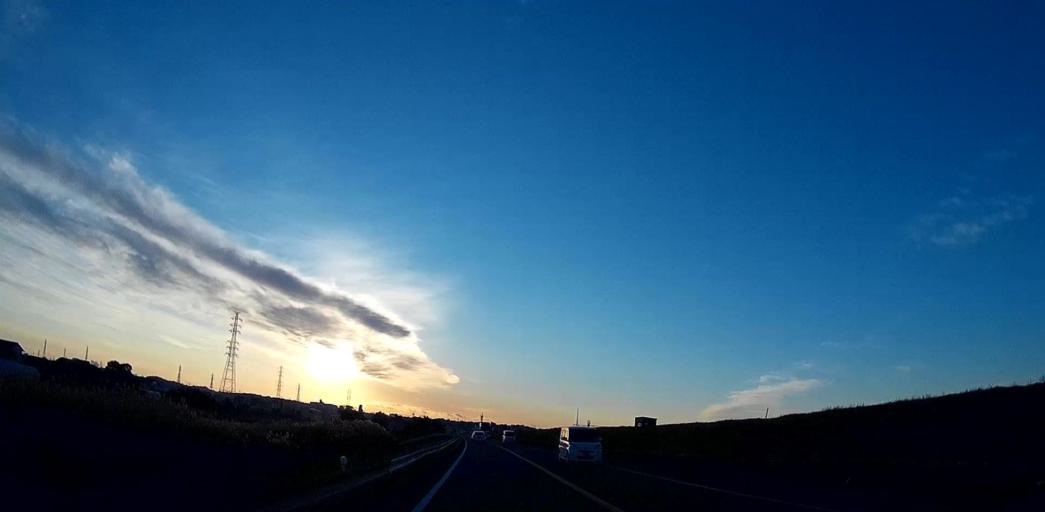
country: JP
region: Chiba
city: Katori-shi
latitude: 35.8974
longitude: 140.5166
